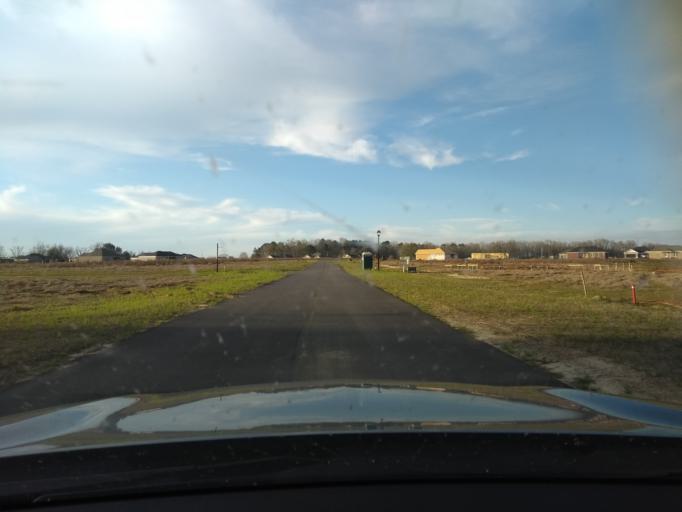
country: US
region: Georgia
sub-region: Bulloch County
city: Statesboro
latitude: 32.3551
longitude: -81.7671
